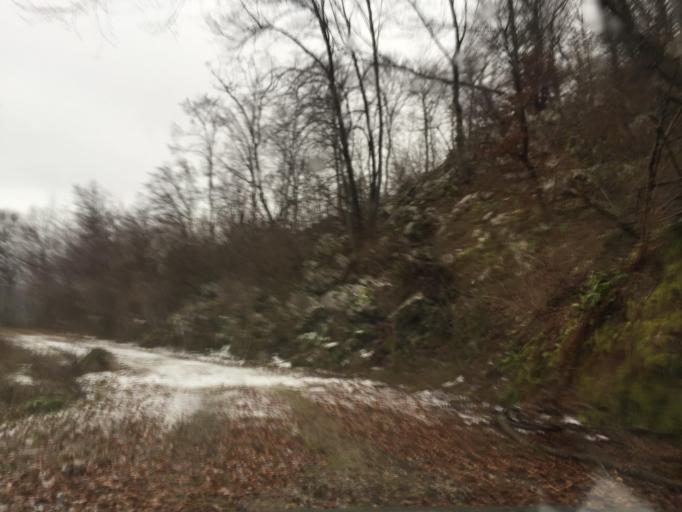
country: SI
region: Kanal
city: Kanal
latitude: 46.0679
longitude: 13.6698
